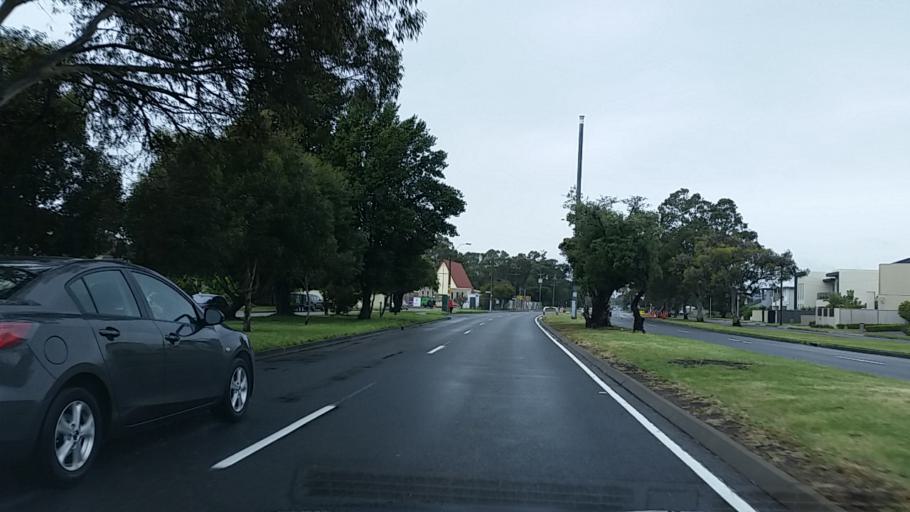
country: AU
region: South Australia
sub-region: Charles Sturt
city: Henley Beach
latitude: -34.9361
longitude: 138.5068
